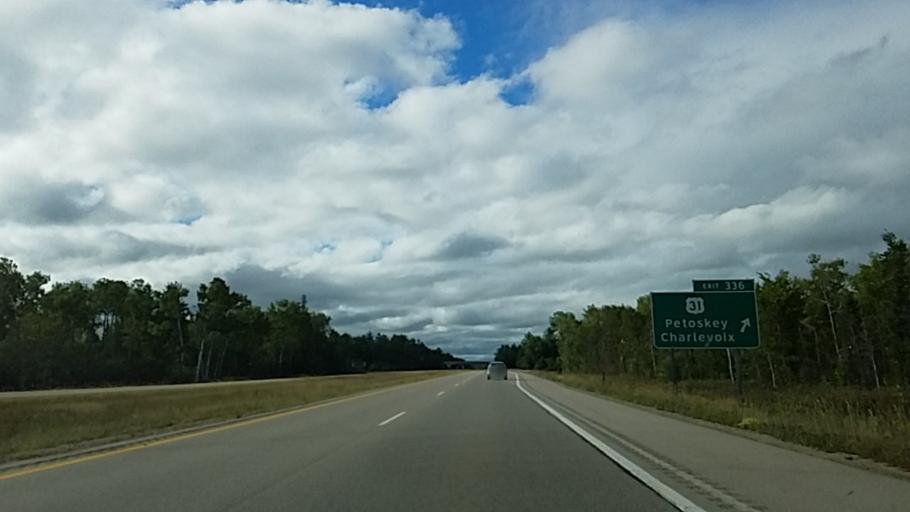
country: US
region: Michigan
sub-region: Mackinac County
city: Saint Ignace
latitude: 45.7394
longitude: -84.7289
